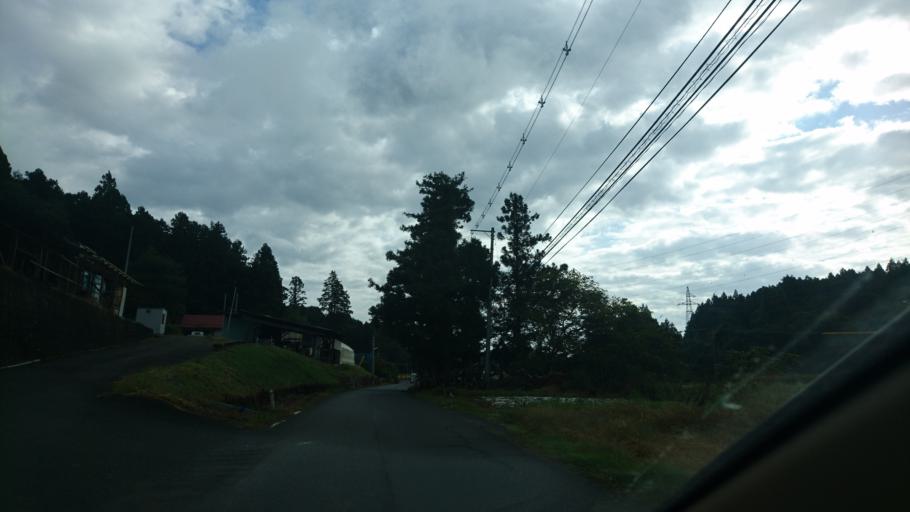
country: JP
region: Iwate
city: Ichinoseki
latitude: 38.7913
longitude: 140.9885
